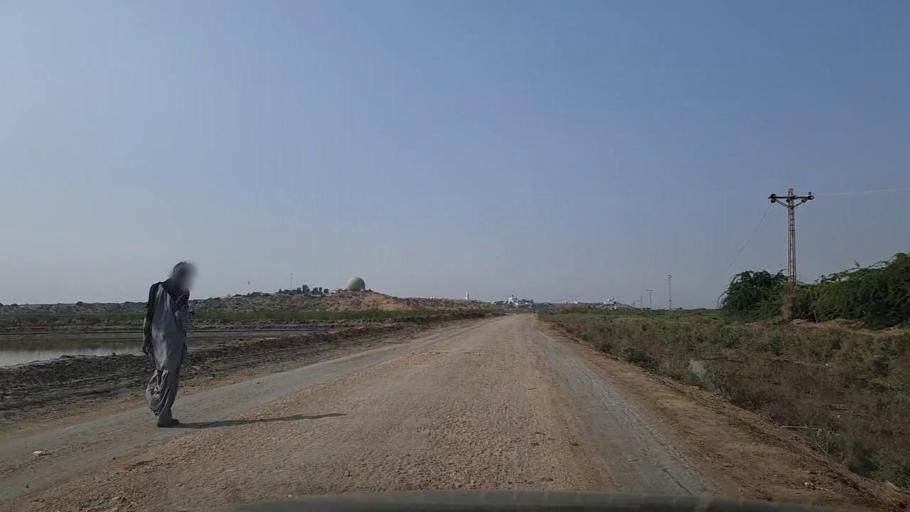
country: PK
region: Sindh
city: Chuhar Jamali
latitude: 24.5503
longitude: 67.8948
